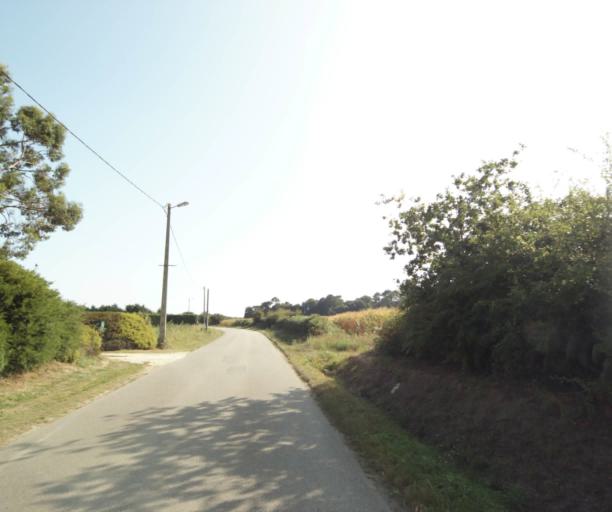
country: FR
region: Brittany
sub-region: Departement du Morbihan
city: Riantec
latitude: 47.7239
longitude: -3.2963
